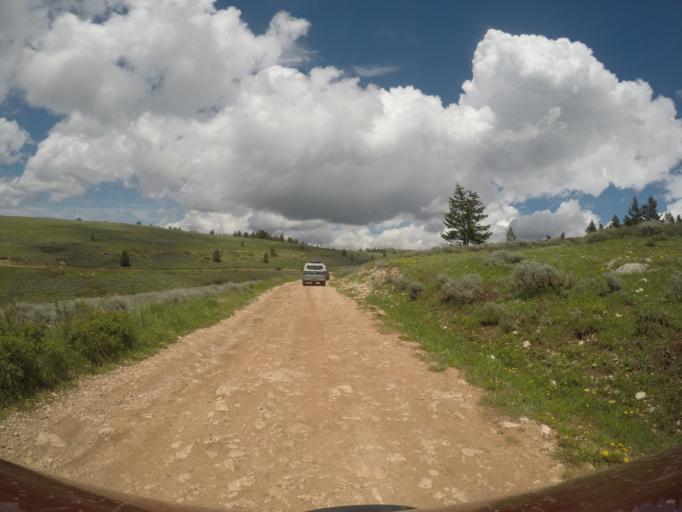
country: US
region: Wyoming
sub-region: Big Horn County
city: Lovell
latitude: 45.1795
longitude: -108.4369
